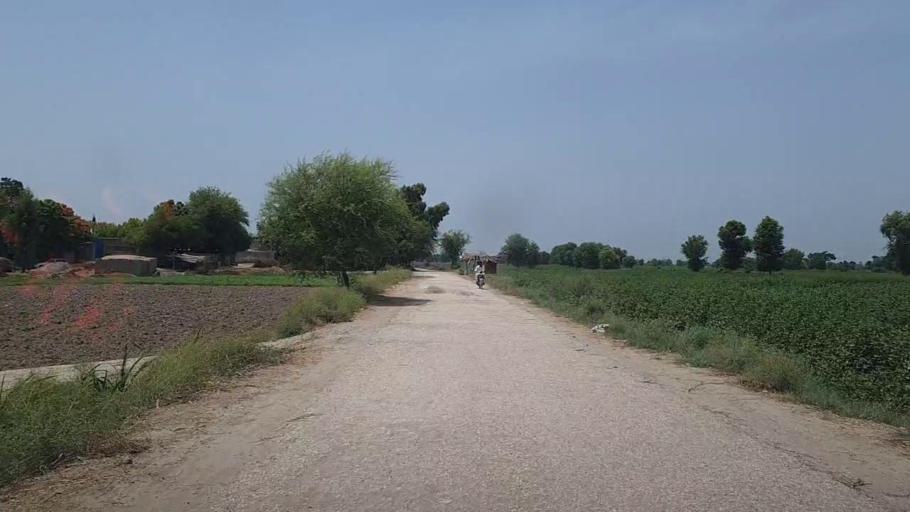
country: PK
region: Sindh
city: Pano Aqil
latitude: 27.8316
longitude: 69.1933
